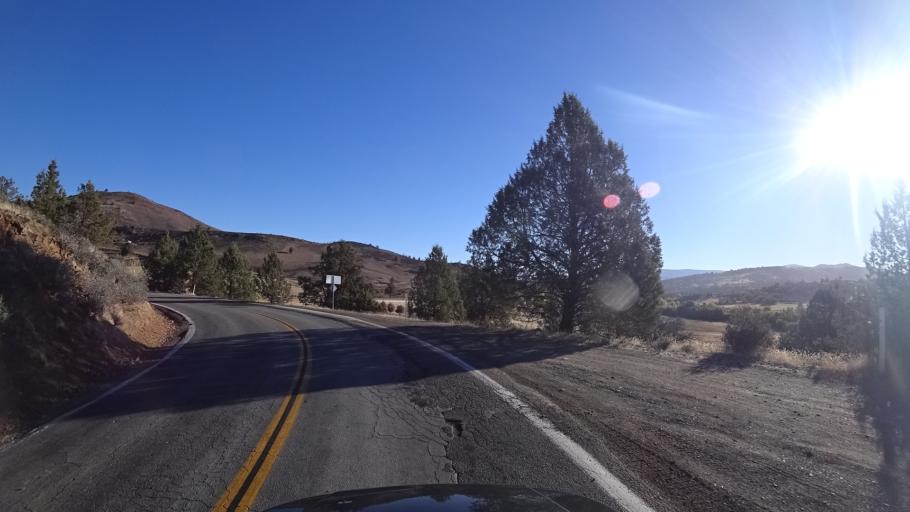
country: US
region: California
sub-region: Siskiyou County
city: Montague
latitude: 41.8986
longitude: -122.5026
